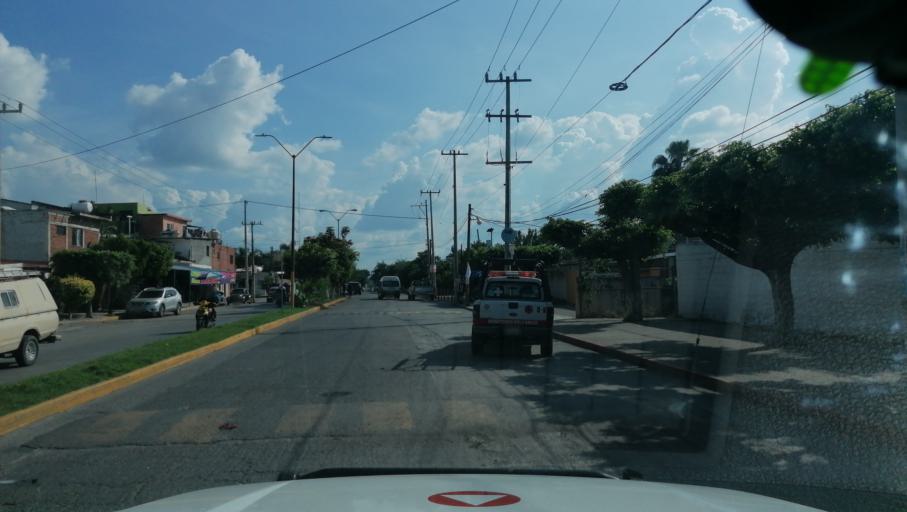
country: MX
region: Morelos
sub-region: Ayala
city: San Pedro Apatlaco
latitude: 18.8099
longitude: -98.9625
